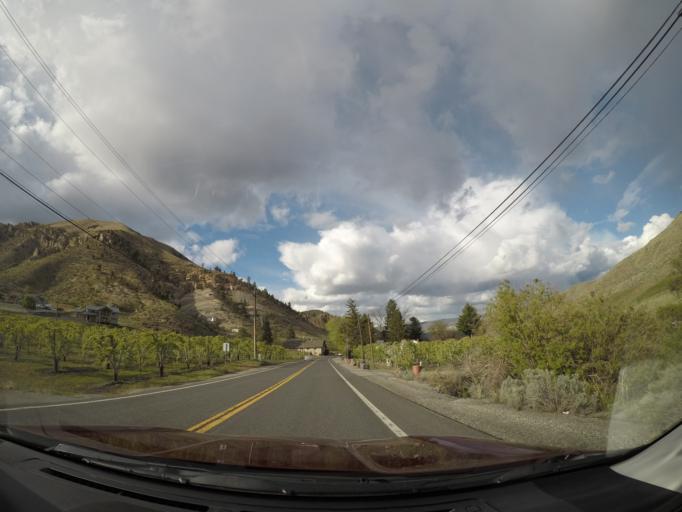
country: US
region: Washington
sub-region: Chelan County
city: South Wenatchee
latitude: 47.3729
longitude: -120.3224
